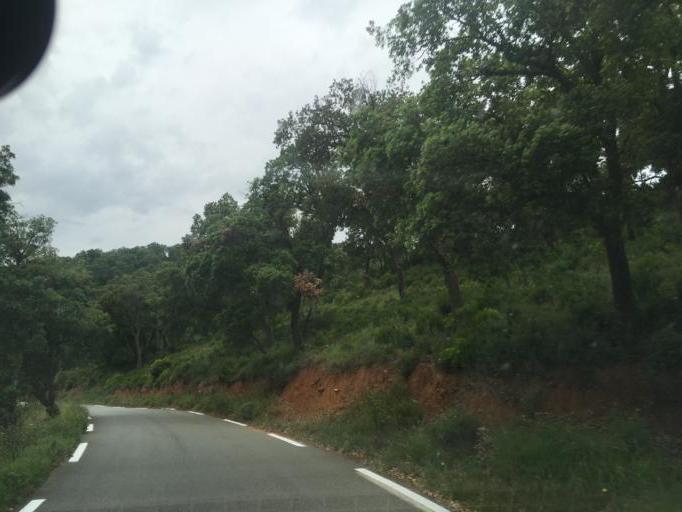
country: FR
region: Provence-Alpes-Cote d'Azur
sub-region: Departement du Var
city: Pierrefeu-du-Var
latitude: 43.2116
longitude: 6.2148
